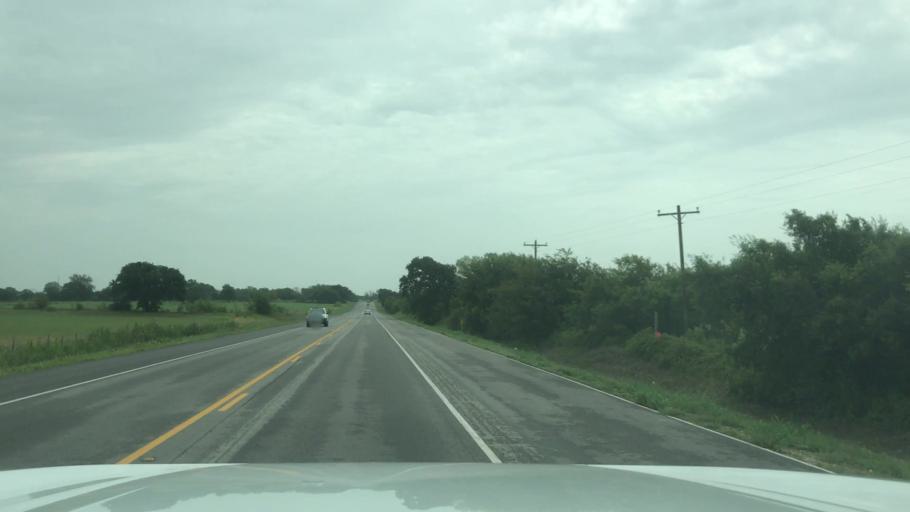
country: US
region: Texas
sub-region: Eastland County
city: Gorman
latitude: 32.2219
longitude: -98.6937
